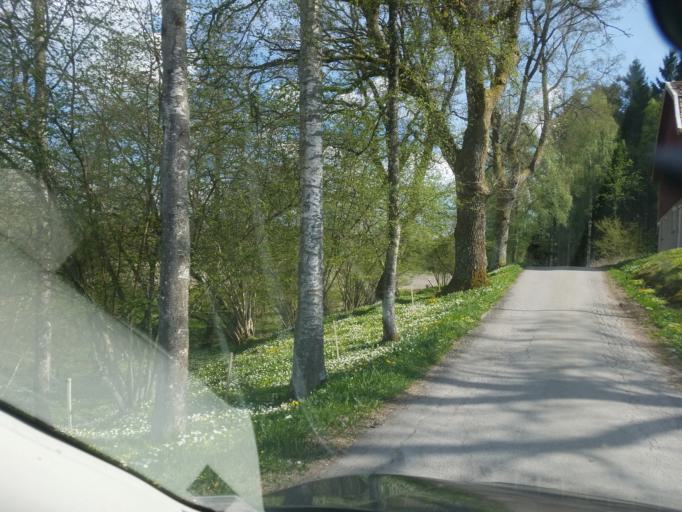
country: SE
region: Vaestra Goetaland
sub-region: Orust
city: Henan
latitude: 58.2935
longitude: 11.5834
